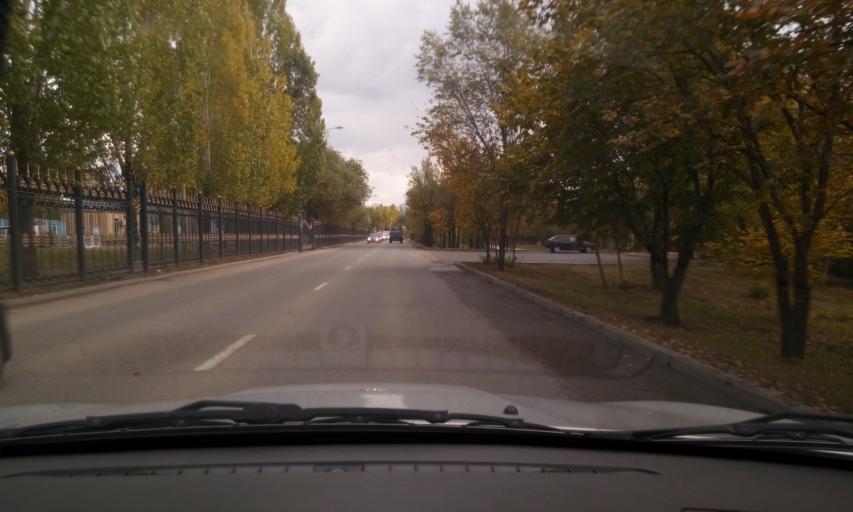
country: KZ
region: Astana Qalasy
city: Astana
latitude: 51.1521
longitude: 71.4177
